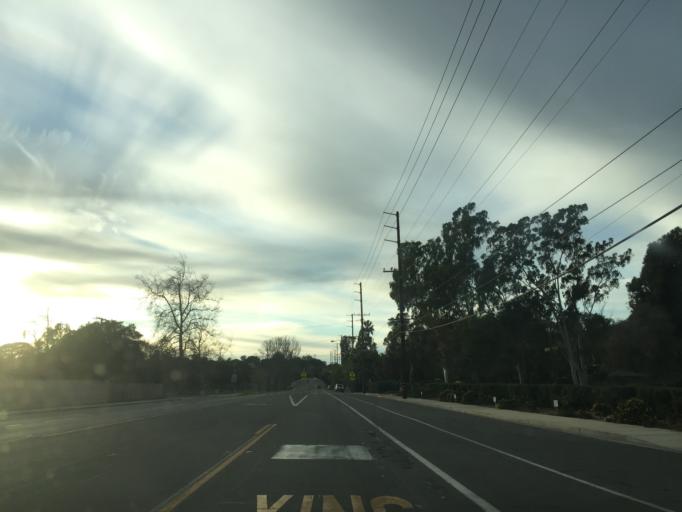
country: US
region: California
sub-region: Santa Barbara County
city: Goleta
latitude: 34.4516
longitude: -119.7988
